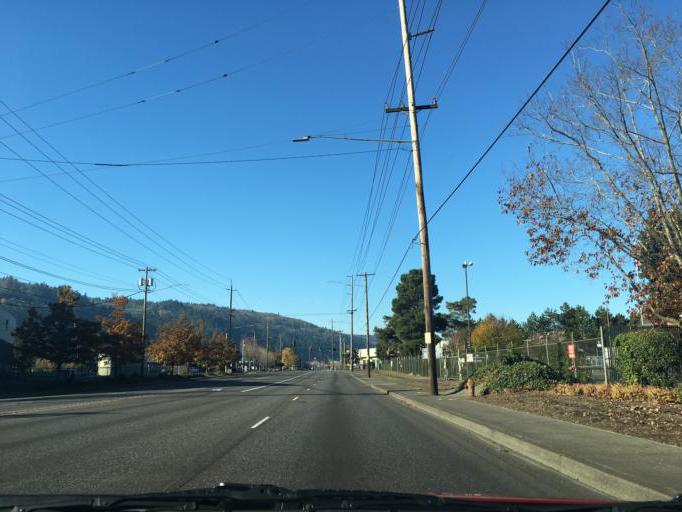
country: US
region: Oregon
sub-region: Multnomah County
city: Portland
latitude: 45.5460
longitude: -122.7088
